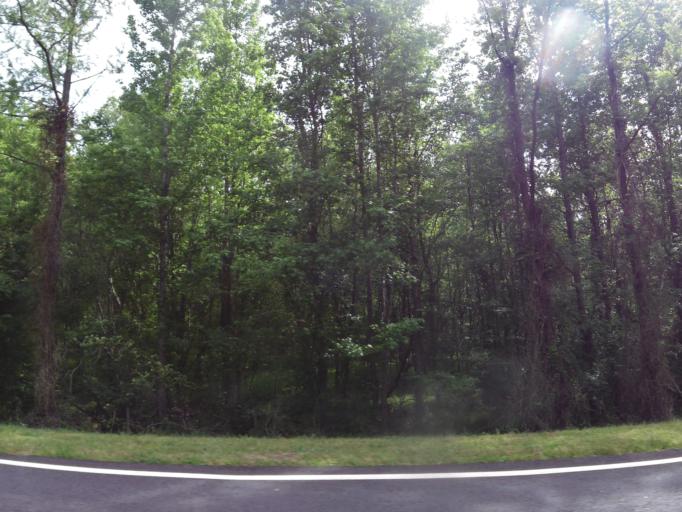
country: US
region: Georgia
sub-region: McDuffie County
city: Thomson
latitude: 33.5332
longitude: -82.4880
